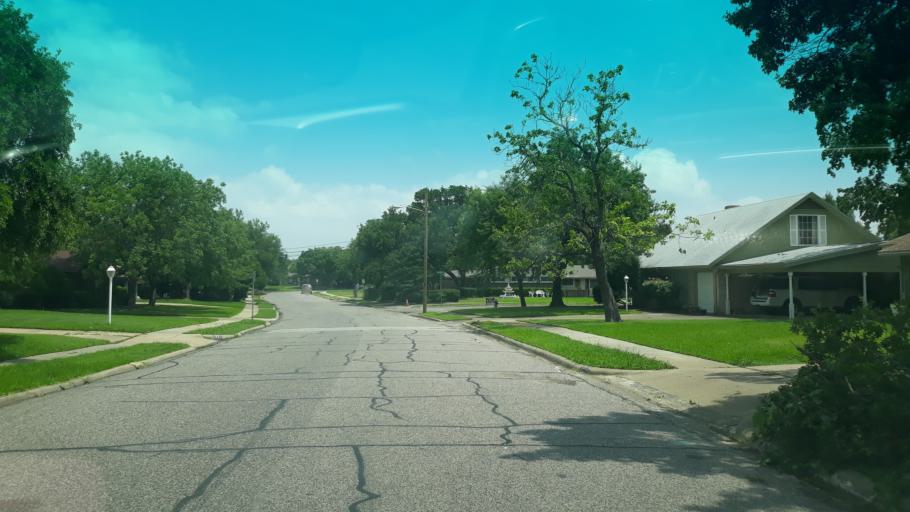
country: US
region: Texas
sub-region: Dallas County
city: Irving
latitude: 32.8551
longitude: -96.9624
